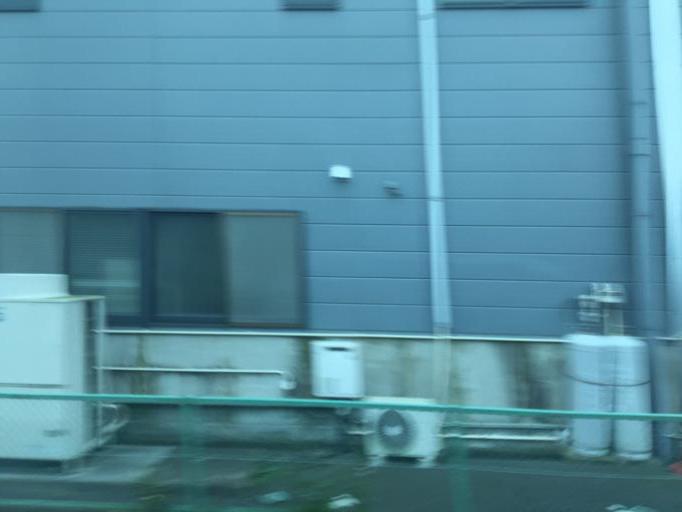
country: JP
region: Ibaraki
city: Shimodate
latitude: 36.2990
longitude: 139.9419
